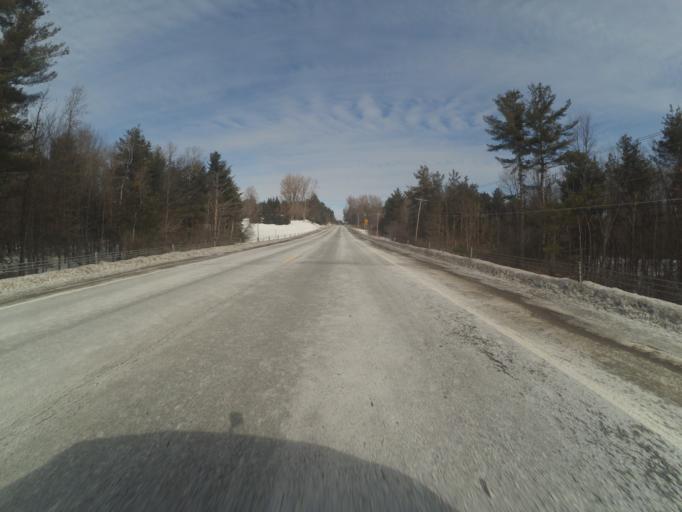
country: US
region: New York
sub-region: St. Lawrence County
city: Hannawa Falls
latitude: 44.6230
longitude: -74.9639
